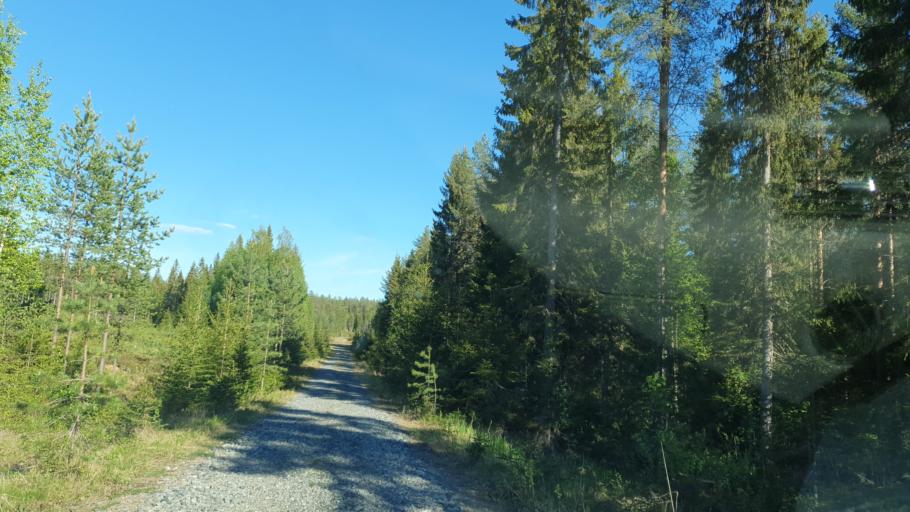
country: FI
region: Kainuu
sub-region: Kehys-Kainuu
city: Kuhmo
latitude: 64.1793
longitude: 29.4198
